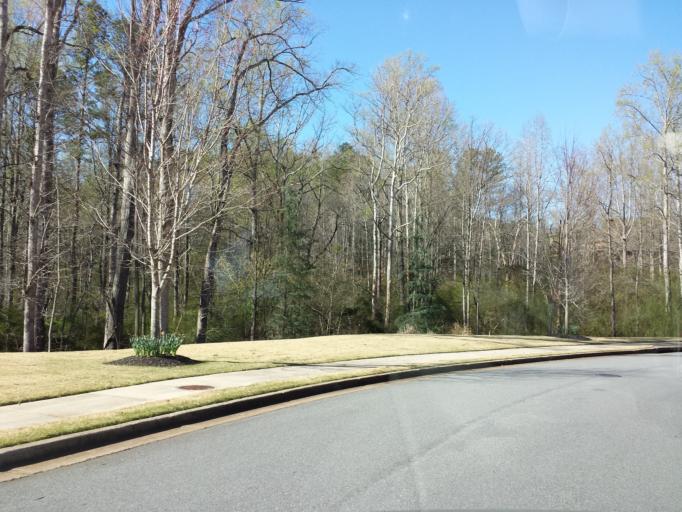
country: US
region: Georgia
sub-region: Cobb County
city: Marietta
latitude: 33.9590
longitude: -84.5790
